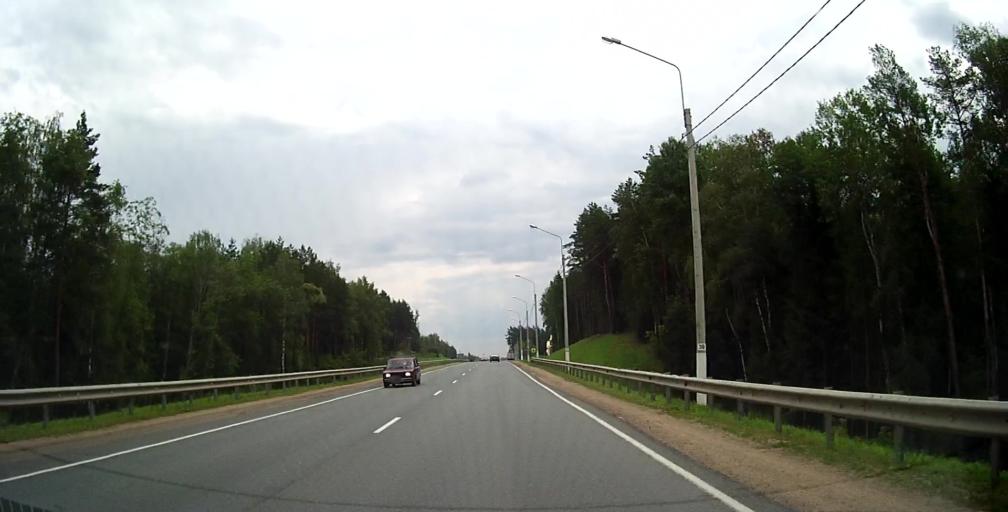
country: RU
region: Smolensk
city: Katyn'
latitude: 54.7748
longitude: 31.7817
